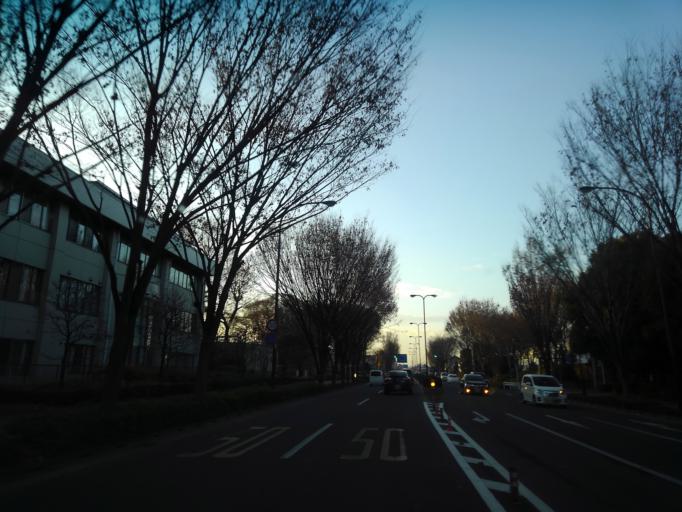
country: JP
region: Tokyo
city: Kokubunji
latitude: 35.6904
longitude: 139.4600
